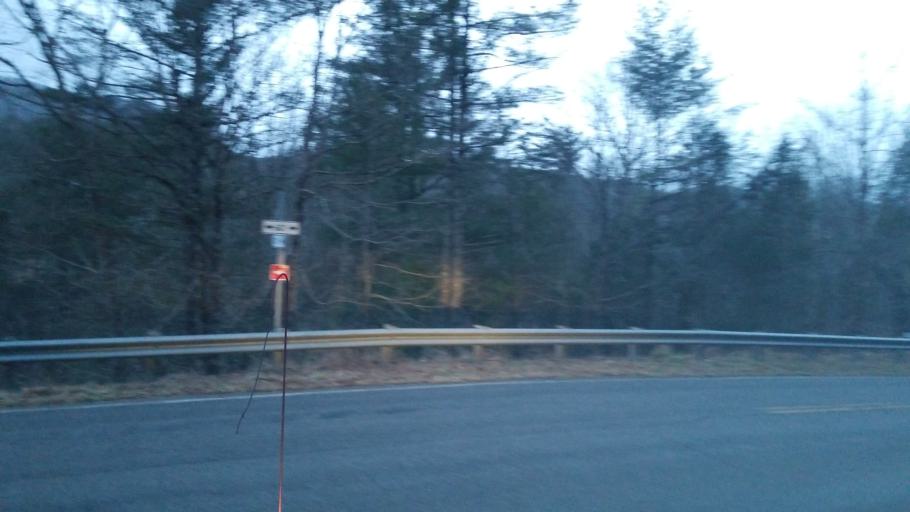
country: US
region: Virginia
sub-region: Pulaski County
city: Pulaski
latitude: 37.1095
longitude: -80.8900
